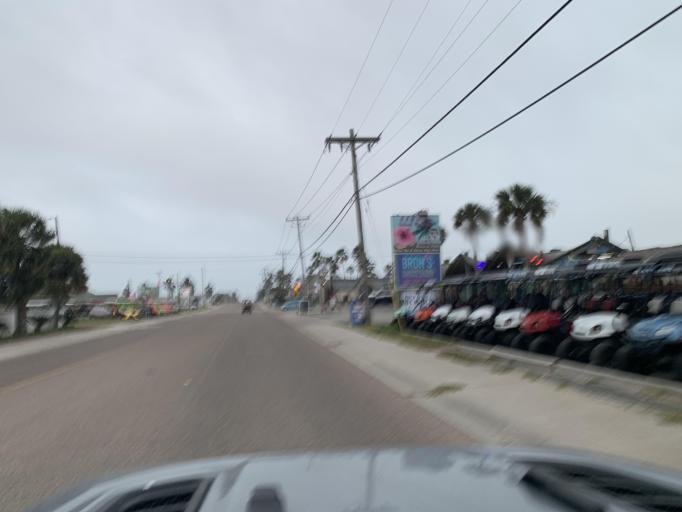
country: US
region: Texas
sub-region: Nueces County
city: Port Aransas
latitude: 27.8270
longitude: -97.0655
